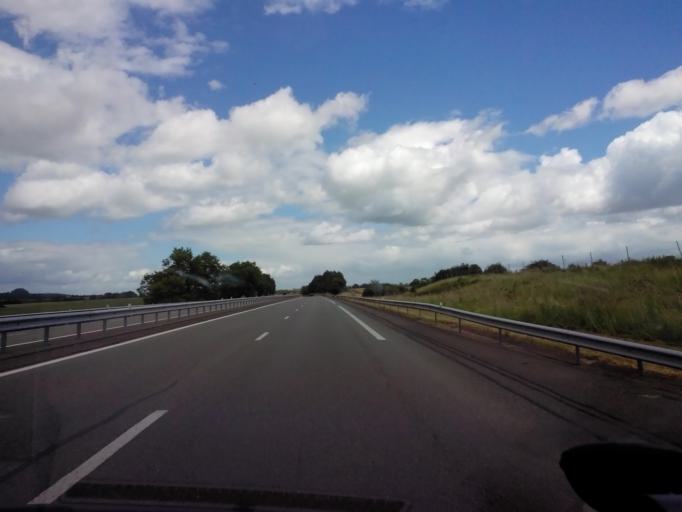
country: FR
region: Champagne-Ardenne
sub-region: Departement de la Haute-Marne
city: Avrecourt
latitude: 48.0234
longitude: 5.5367
